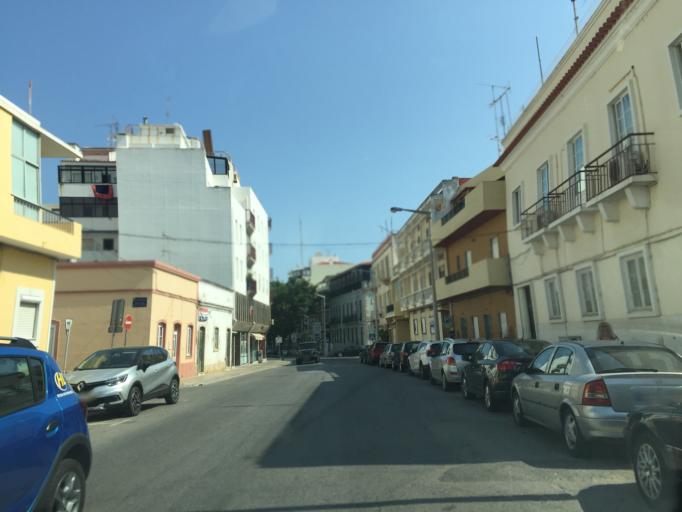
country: PT
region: Faro
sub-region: Faro
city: Faro
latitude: 37.0167
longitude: -7.9291
